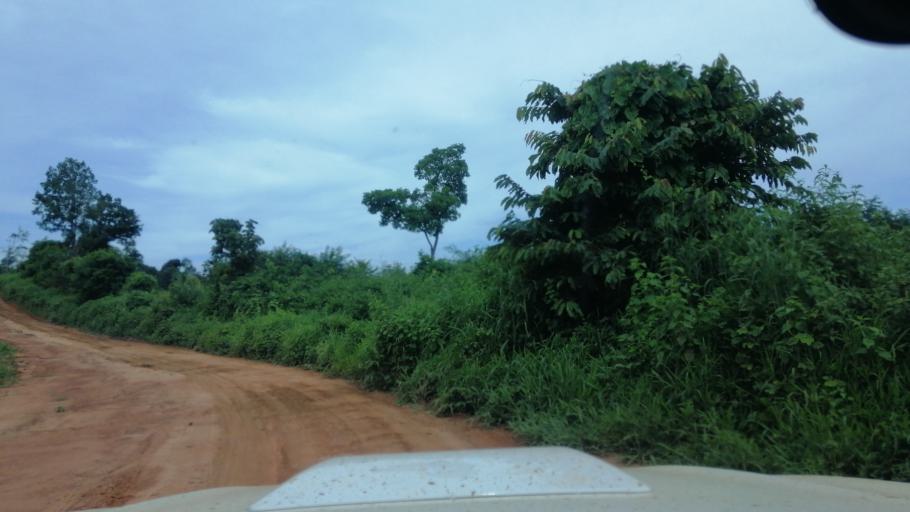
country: TH
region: Loei
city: Na Haeo
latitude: 17.5950
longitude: 101.1296
